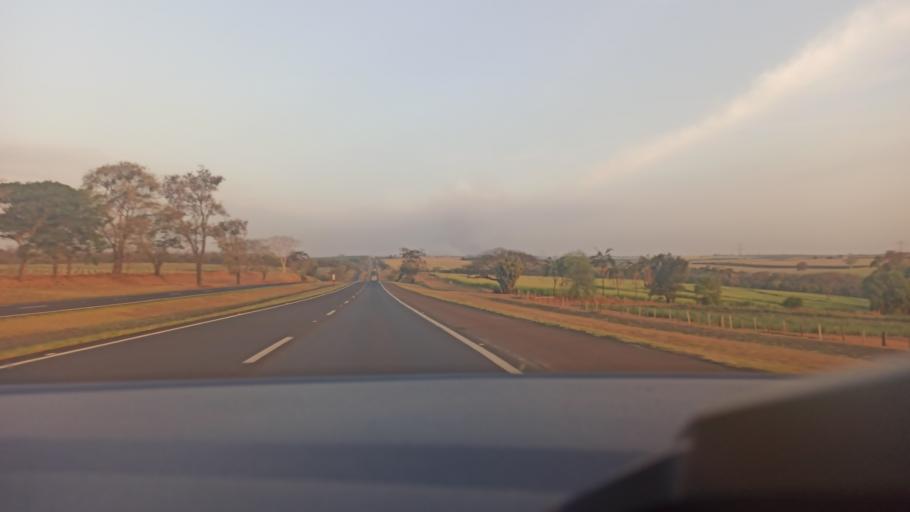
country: BR
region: Sao Paulo
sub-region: Taquaritinga
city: Taquaritinga
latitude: -21.4251
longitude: -48.6718
